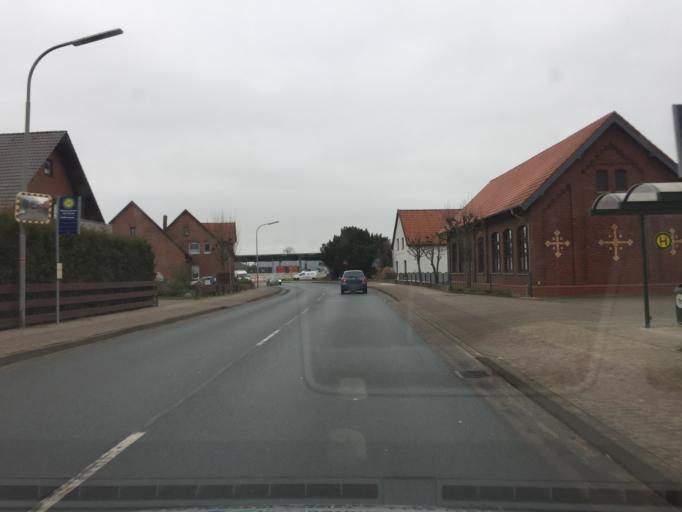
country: DE
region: Lower Saxony
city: Niedernwohren
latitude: 52.3505
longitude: 9.1486
